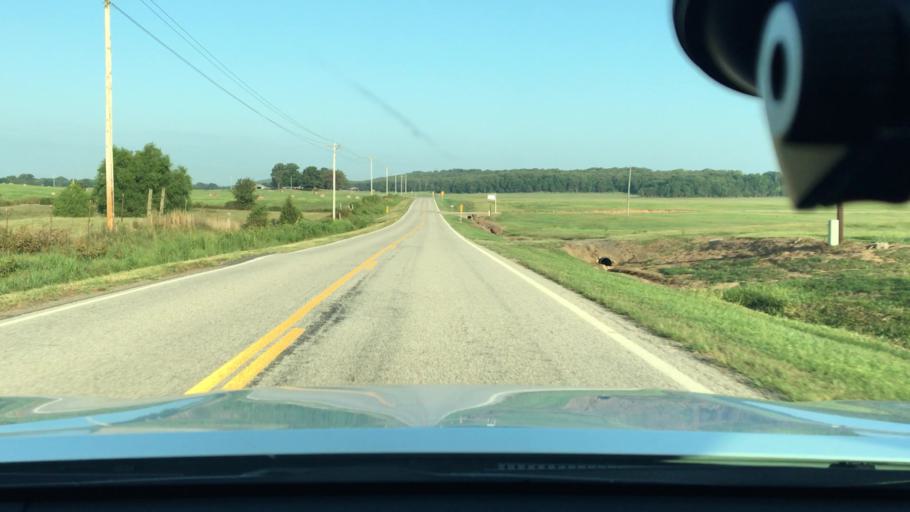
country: US
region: Arkansas
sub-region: Johnson County
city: Coal Hill
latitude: 35.3511
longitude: -93.5825
